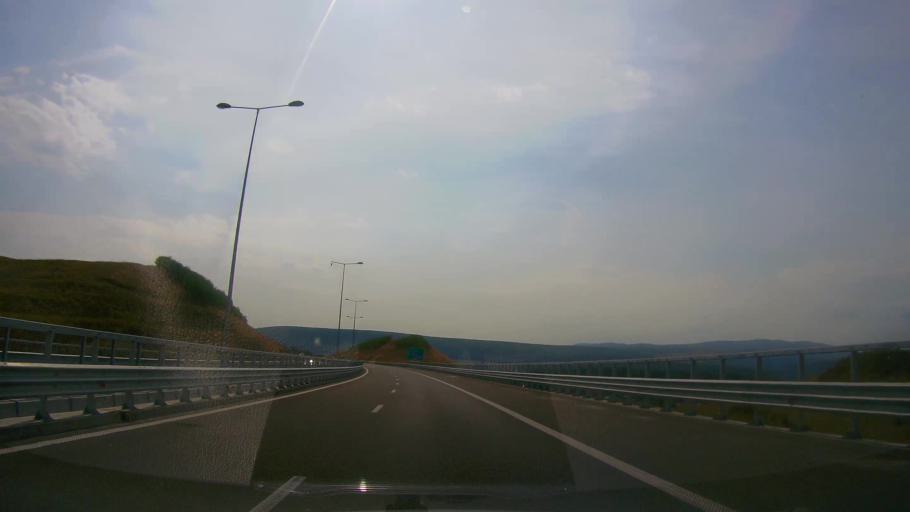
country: RO
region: Cluj
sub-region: Comuna Gilau
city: Gilau
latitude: 46.7674
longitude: 23.3836
